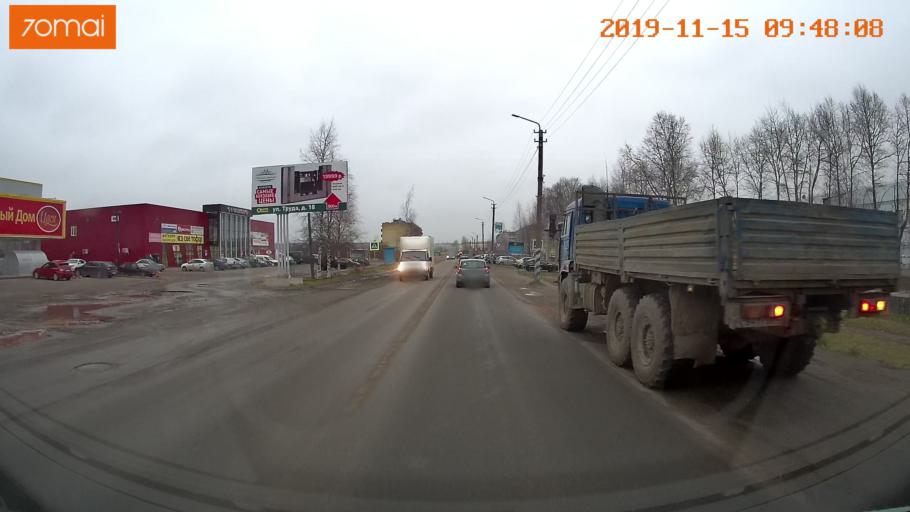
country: RU
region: Vologda
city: Sheksna
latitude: 59.2211
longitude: 38.5120
